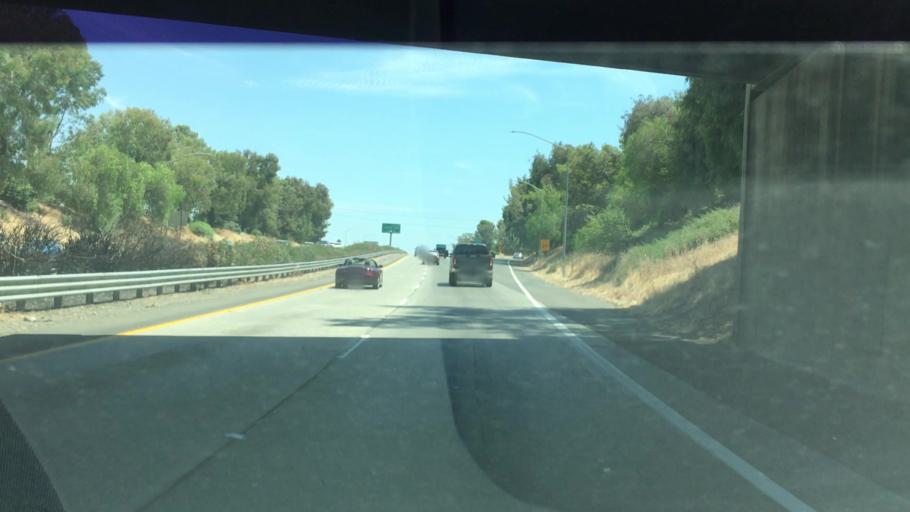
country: US
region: California
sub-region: Sacramento County
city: Galt
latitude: 38.2643
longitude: -121.3001
